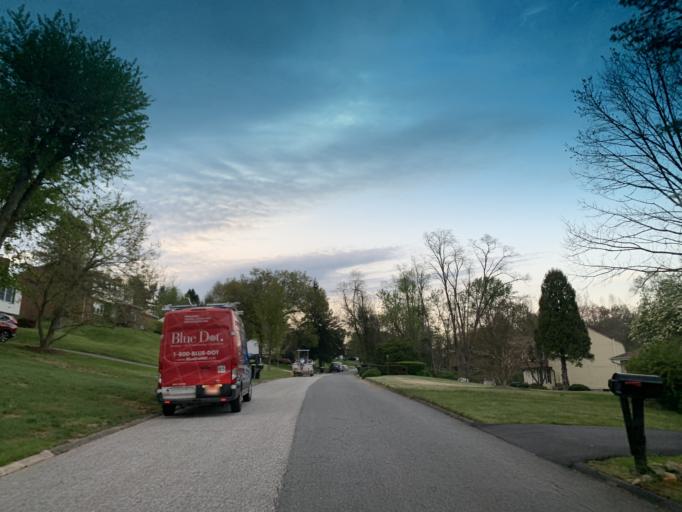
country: US
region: Maryland
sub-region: Harford County
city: Bel Air South
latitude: 39.5030
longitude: -76.3448
